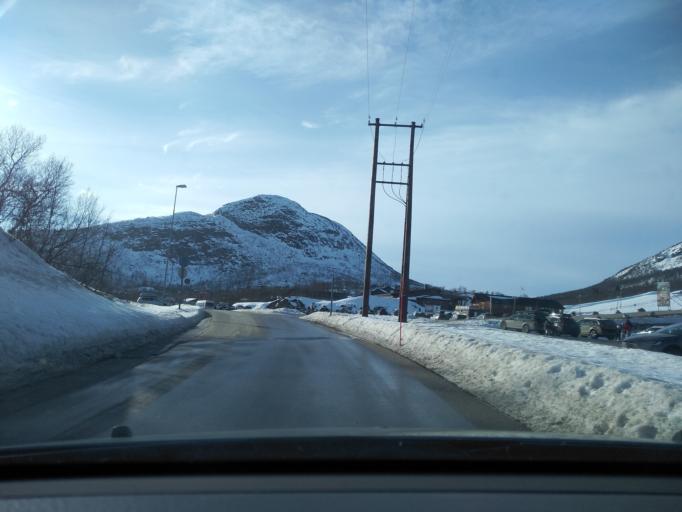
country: NO
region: Aust-Agder
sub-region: Bykle
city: Hovden
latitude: 59.5689
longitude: 7.3524
